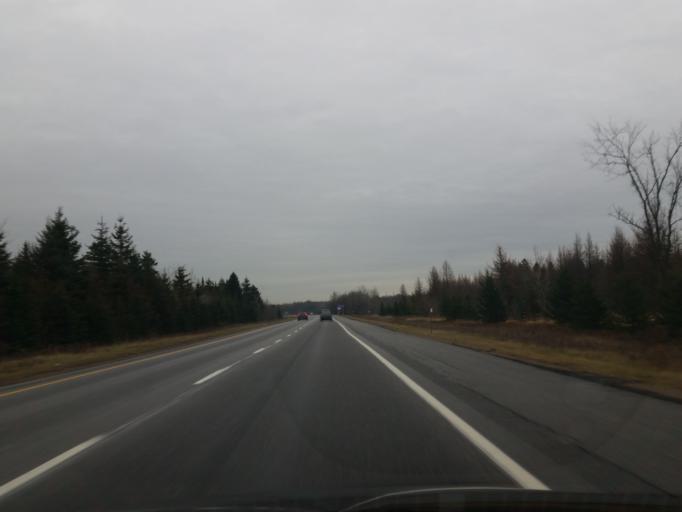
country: CA
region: Quebec
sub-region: Capitale-Nationale
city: Saint-Augustin-de-Desmaures
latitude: 46.7507
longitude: -71.4991
